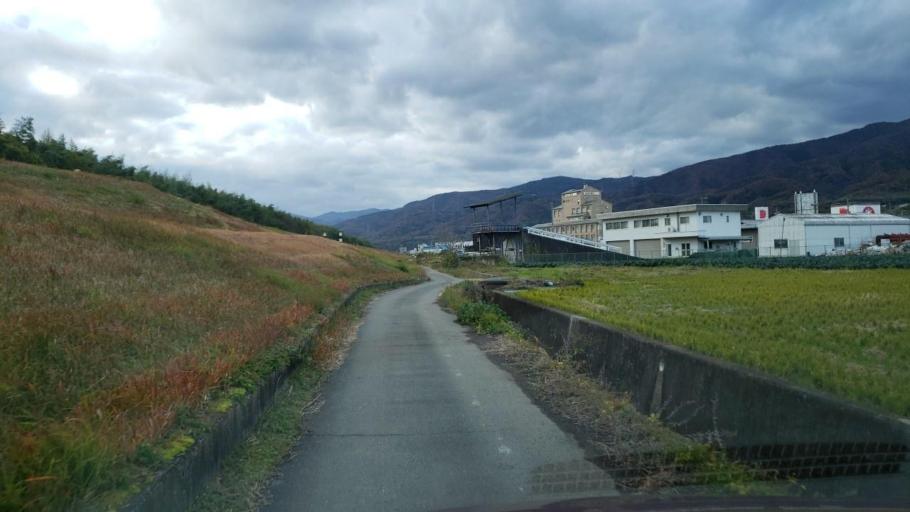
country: JP
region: Tokushima
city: Wakimachi
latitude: 34.0624
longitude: 134.1590
